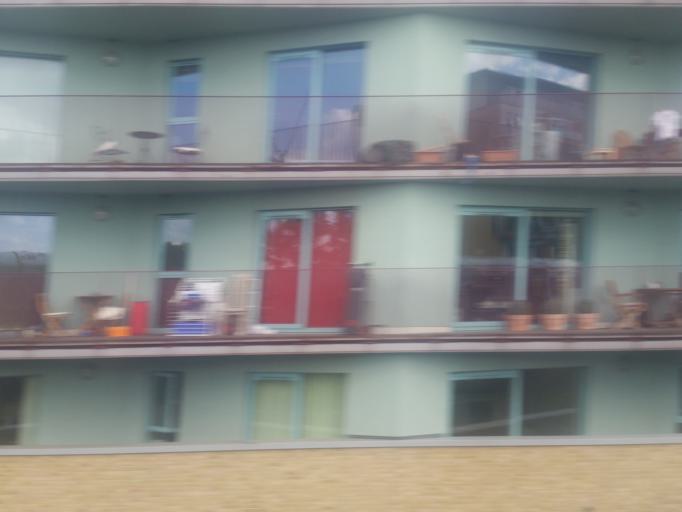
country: GB
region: England
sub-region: Greater London
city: Kennington
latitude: 51.4913
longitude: -0.0989
